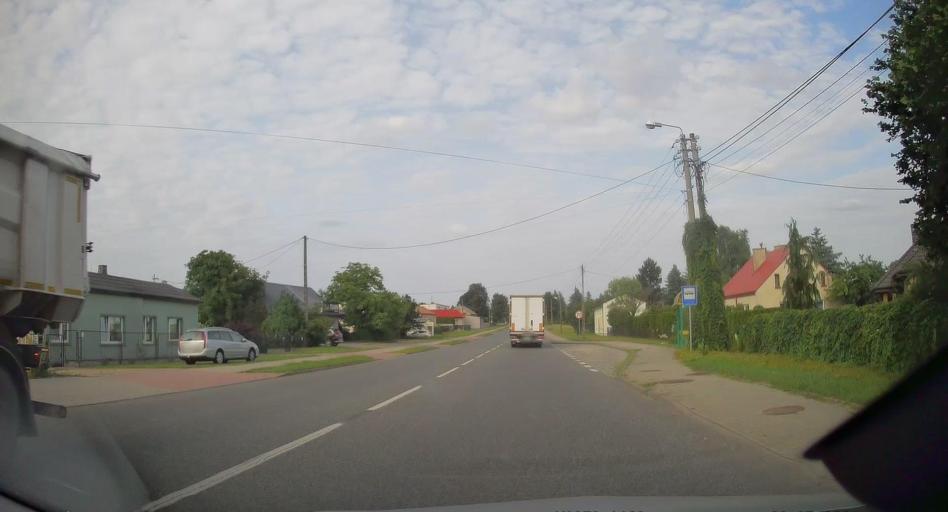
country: PL
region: Silesian Voivodeship
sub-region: Powiat czestochowski
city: Redziny
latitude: 50.8466
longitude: 19.1875
